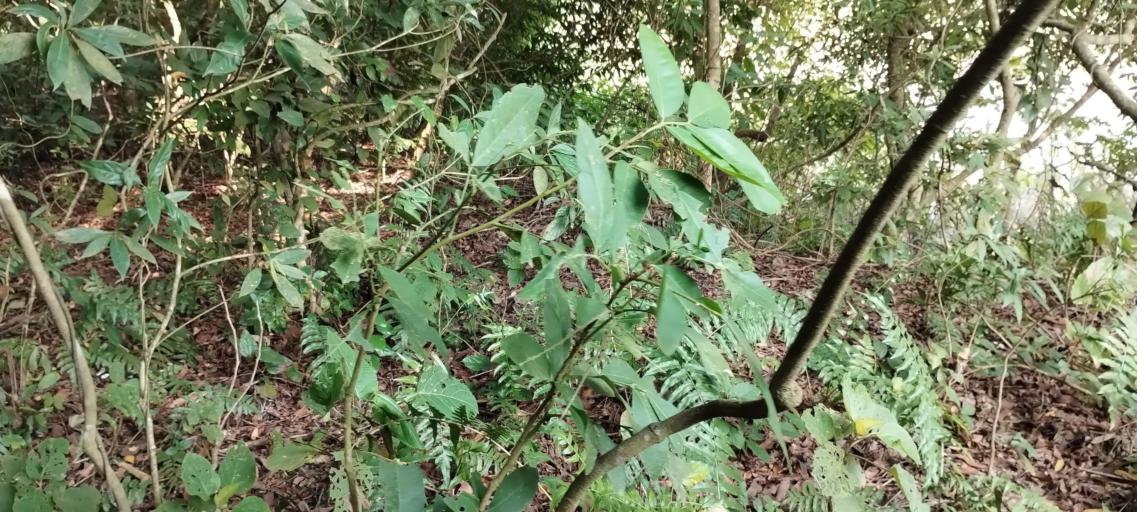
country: NP
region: Far Western
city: Tikapur
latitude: 28.4670
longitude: 81.2484
